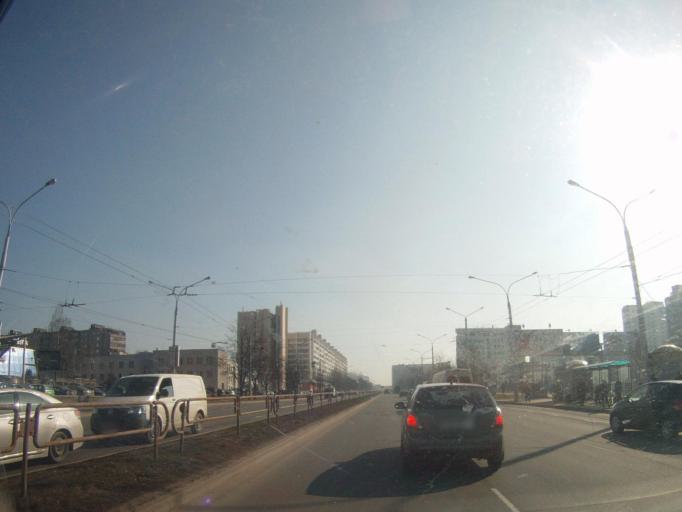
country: BY
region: Minsk
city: Minsk
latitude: 53.9285
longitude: 27.5865
